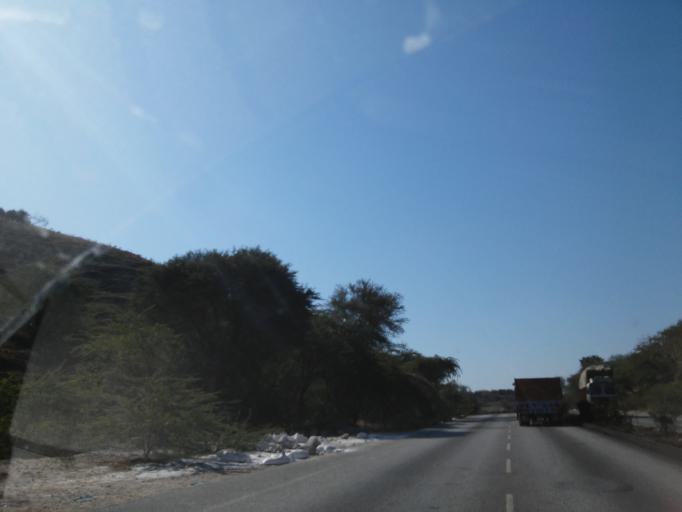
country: IN
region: Rajasthan
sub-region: Udaipur
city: Udaipur
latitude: 24.3074
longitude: 73.6787
